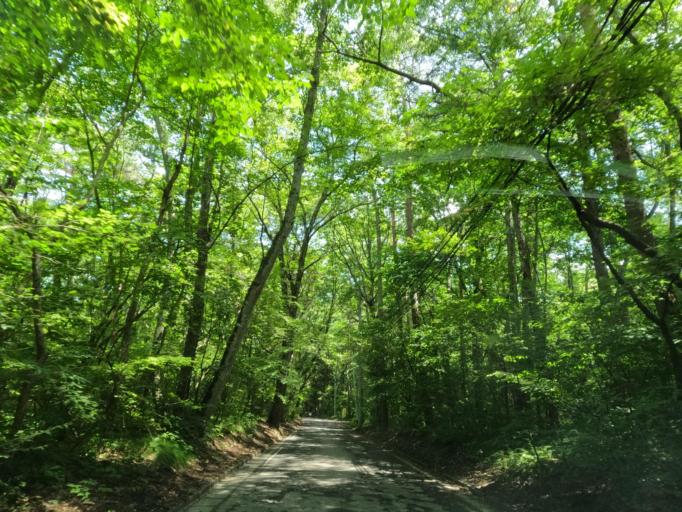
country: JP
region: Nagano
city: Komoro
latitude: 36.3636
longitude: 138.6018
